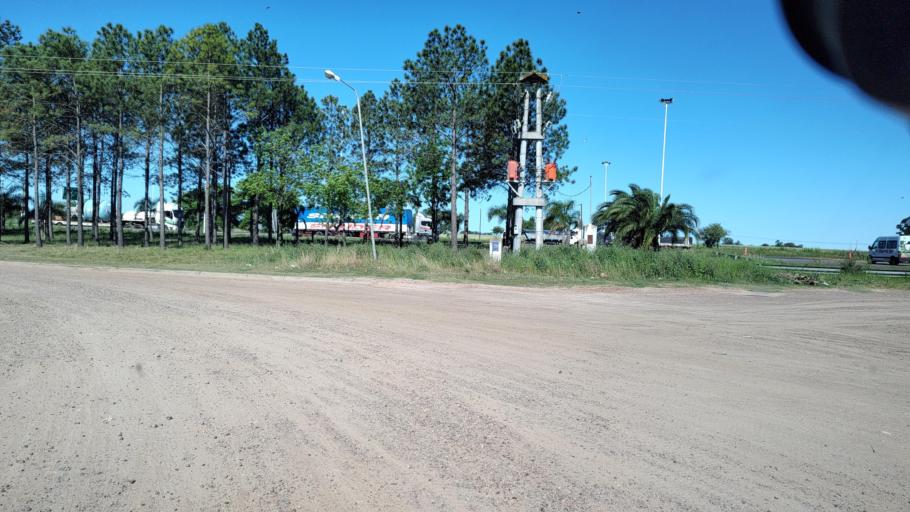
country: AR
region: Entre Rios
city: Colonia Elia
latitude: -32.6663
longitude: -58.4424
